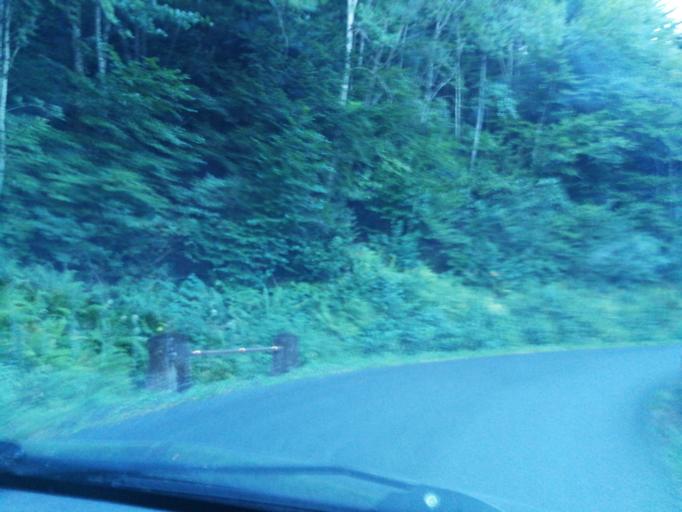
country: FR
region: Auvergne
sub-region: Departement du Cantal
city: Vic-sur-Cere
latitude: 45.0776
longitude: 2.5673
